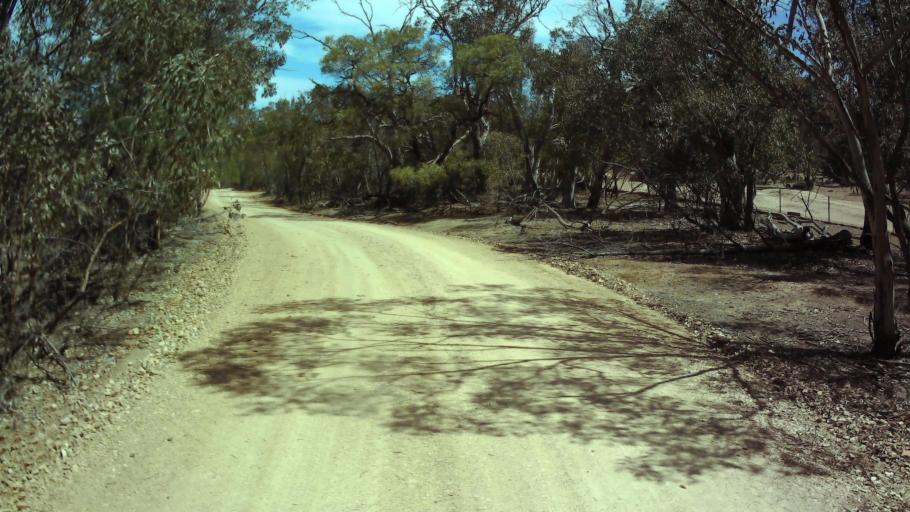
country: AU
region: New South Wales
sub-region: Weddin
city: Grenfell
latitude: -33.8062
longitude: 148.1603
